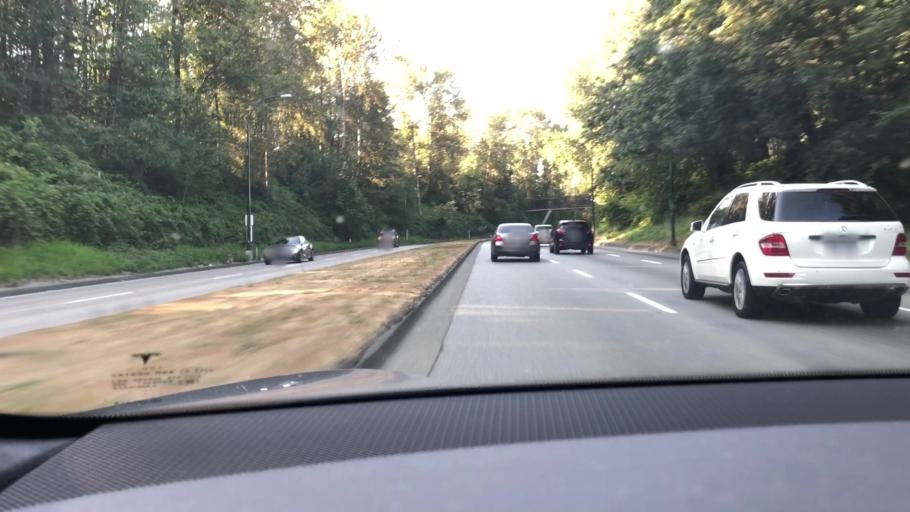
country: CA
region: British Columbia
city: Burnaby
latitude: 49.2093
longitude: -123.0237
